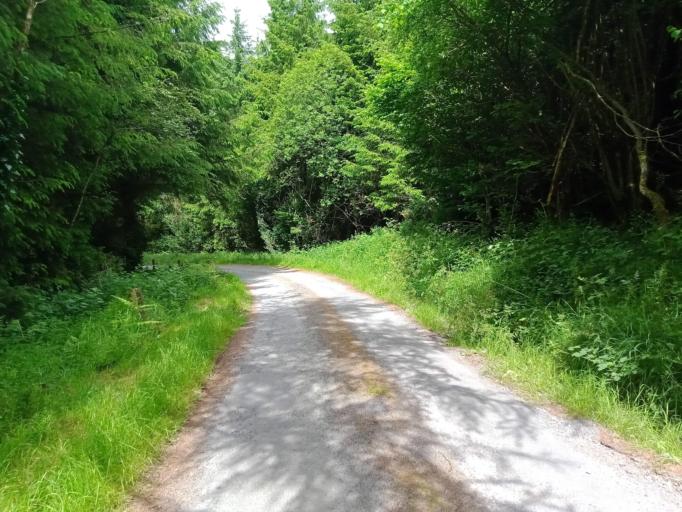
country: IE
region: Leinster
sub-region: Laois
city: Rathdowney
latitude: 52.7935
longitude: -7.4784
